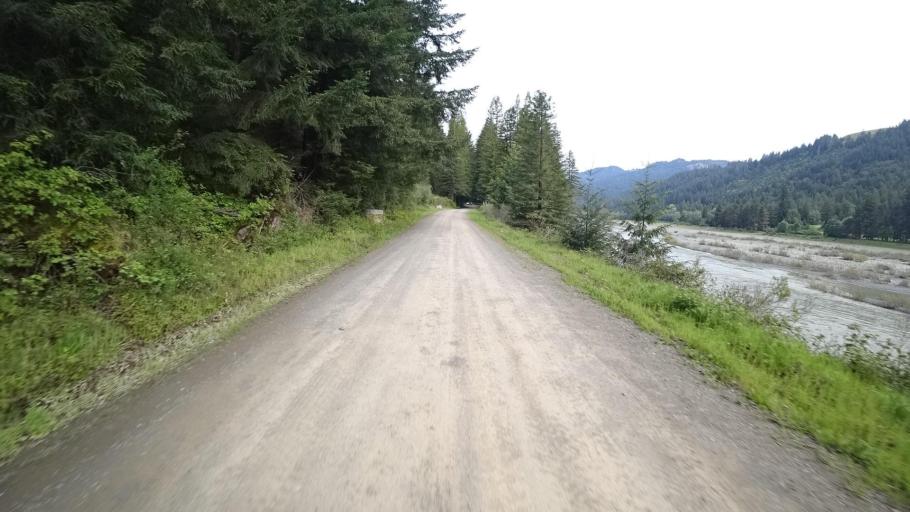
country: US
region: California
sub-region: Humboldt County
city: Redway
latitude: 40.3265
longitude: -123.8408
